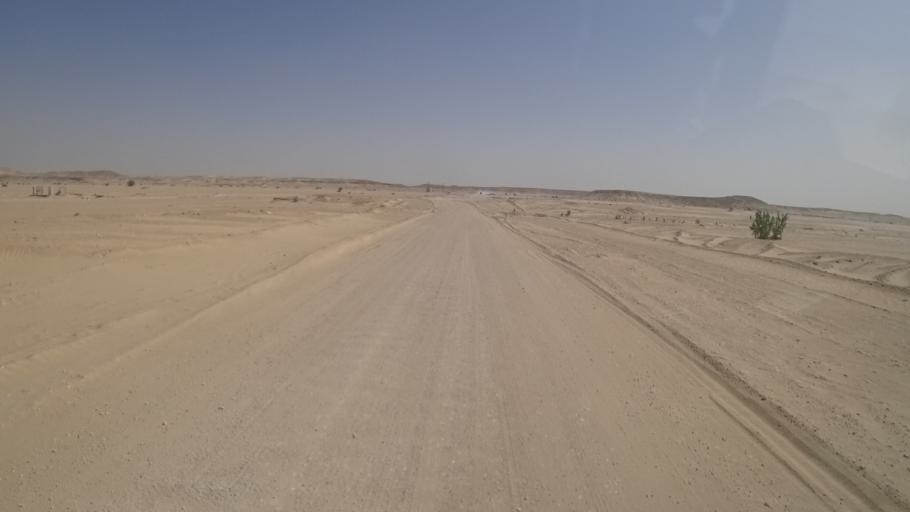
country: YE
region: Al Mahrah
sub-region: Shahan
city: Shihan as Sufla
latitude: 17.8756
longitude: 52.6062
